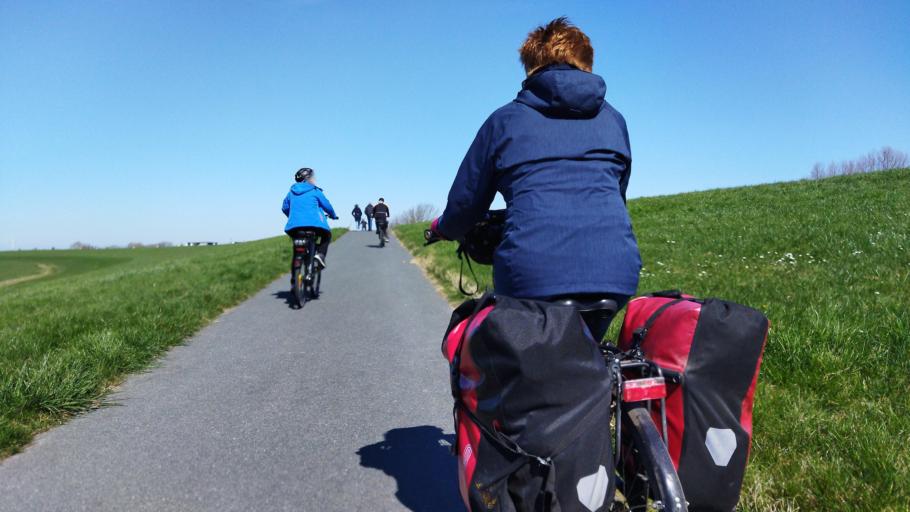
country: DE
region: Lower Saxony
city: Wremen
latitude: 53.6402
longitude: 8.4992
